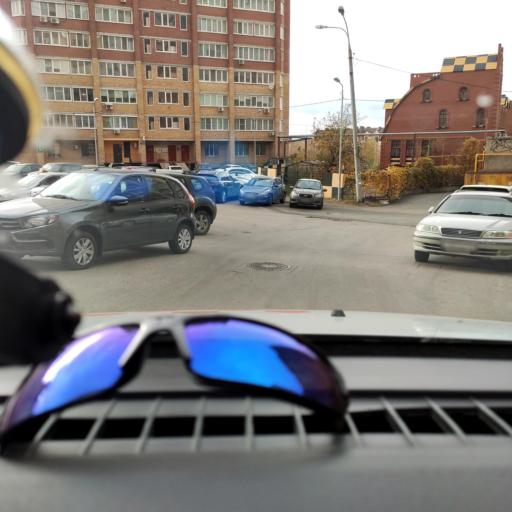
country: RU
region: Samara
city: Samara
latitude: 53.2374
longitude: 50.1804
